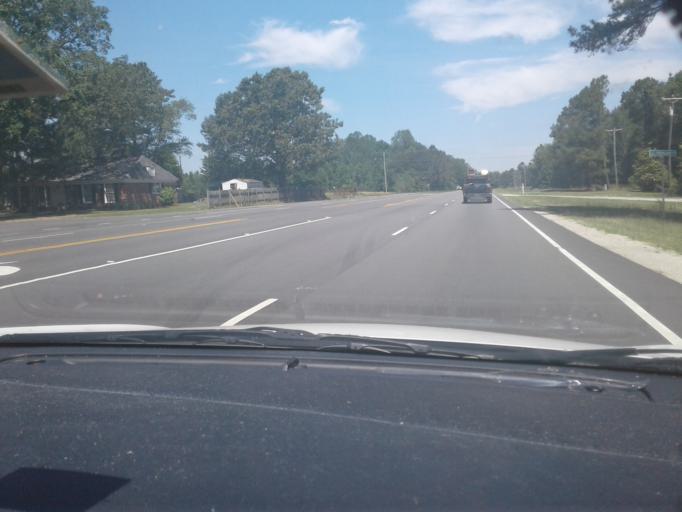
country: US
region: North Carolina
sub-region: Harnett County
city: Buies Creek
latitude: 35.3925
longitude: -78.7288
